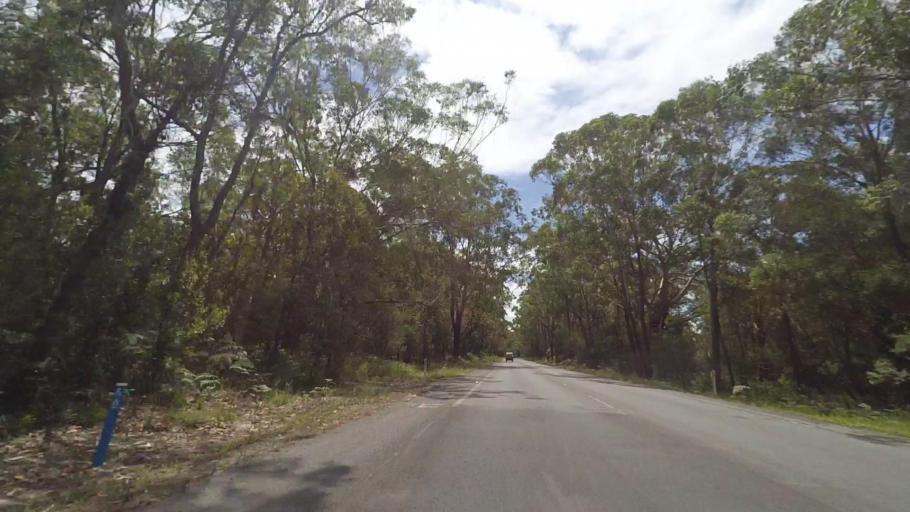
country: AU
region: New South Wales
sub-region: Port Stephens Shire
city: Medowie
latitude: -32.7751
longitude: 151.8719
